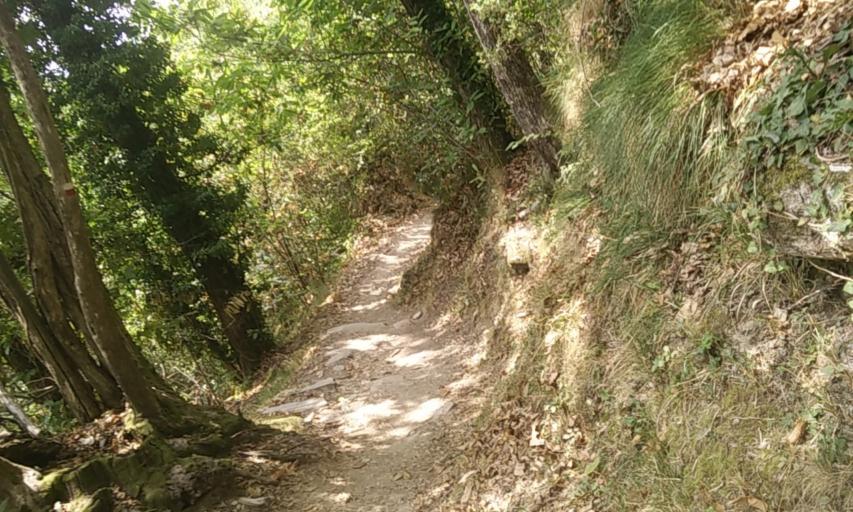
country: IT
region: Tuscany
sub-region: Provincia di Lucca
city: Pontestazzemese
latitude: 43.9948
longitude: 10.3320
